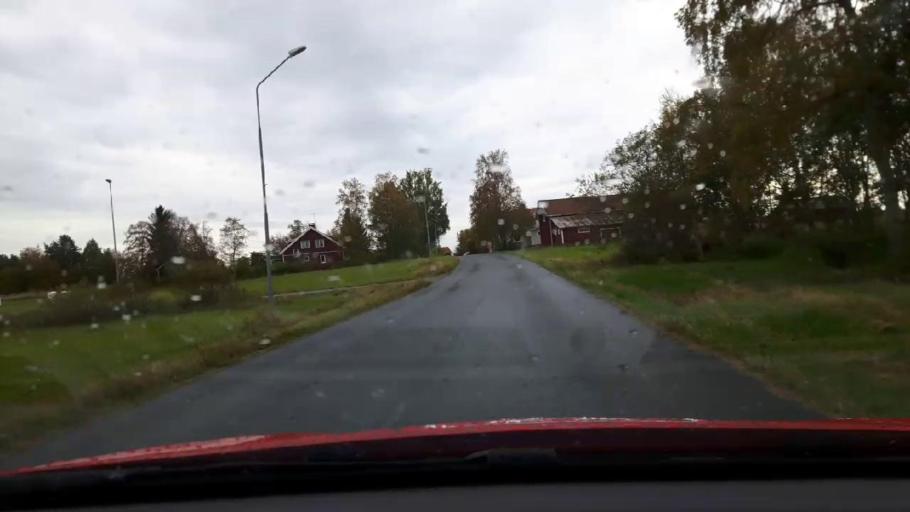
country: SE
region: Jaemtland
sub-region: Bergs Kommun
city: Hoverberg
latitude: 62.9216
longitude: 14.5168
